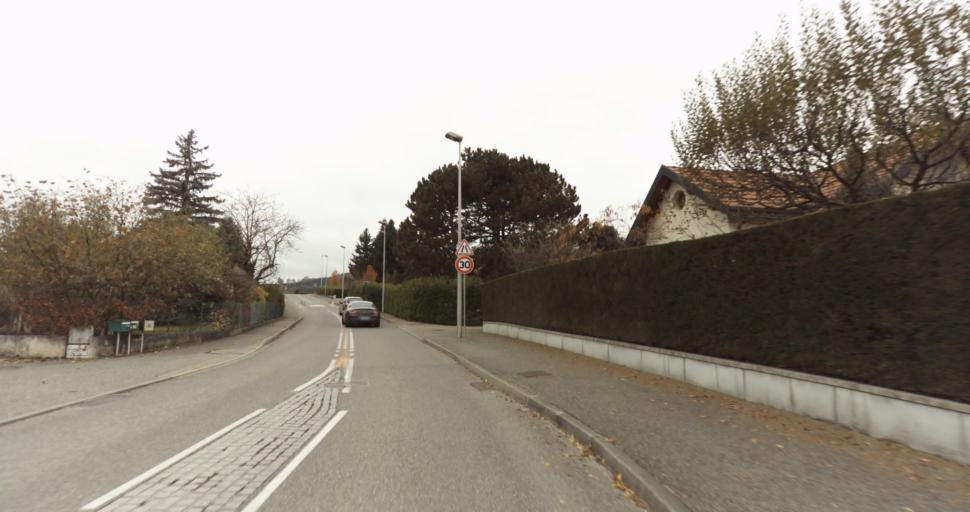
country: FR
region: Rhone-Alpes
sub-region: Departement de la Haute-Savoie
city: Metz-Tessy
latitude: 45.9454
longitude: 6.1076
